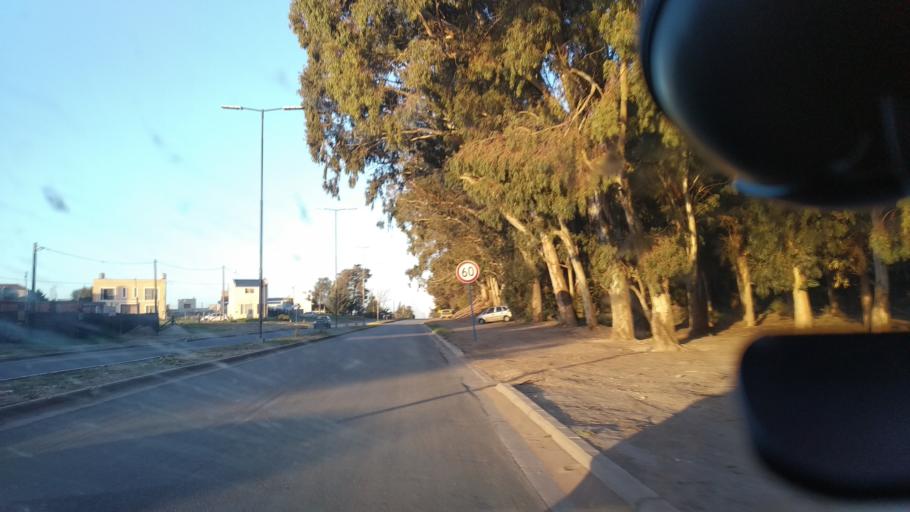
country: AR
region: Buenos Aires
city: Necochea
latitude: -38.5866
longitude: -58.7535
